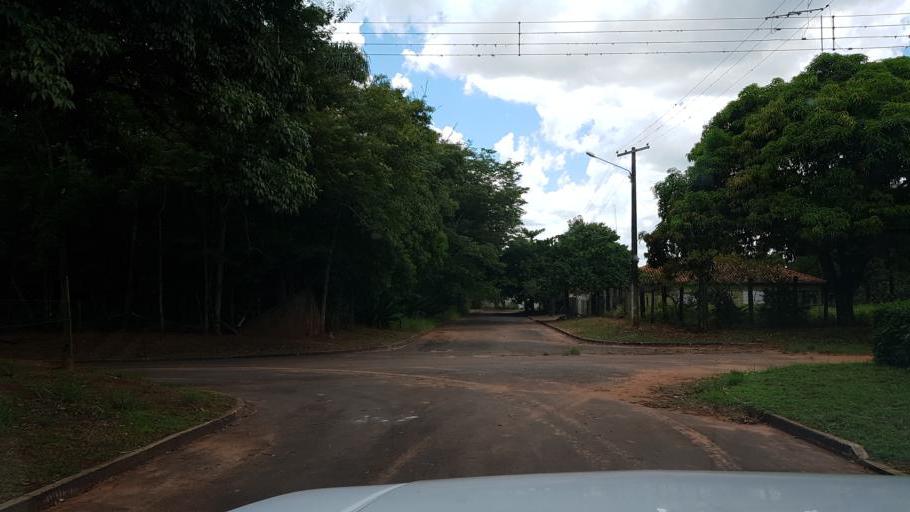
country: BR
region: Sao Paulo
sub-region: Paraguacu Paulista
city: Paraguacu Paulista
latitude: -22.3527
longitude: -50.6223
